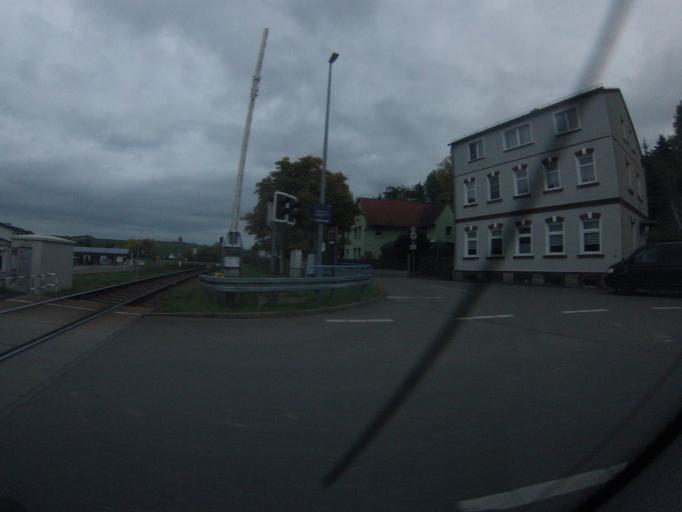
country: DE
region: Thuringia
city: Saara
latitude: 50.9210
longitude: 12.3910
